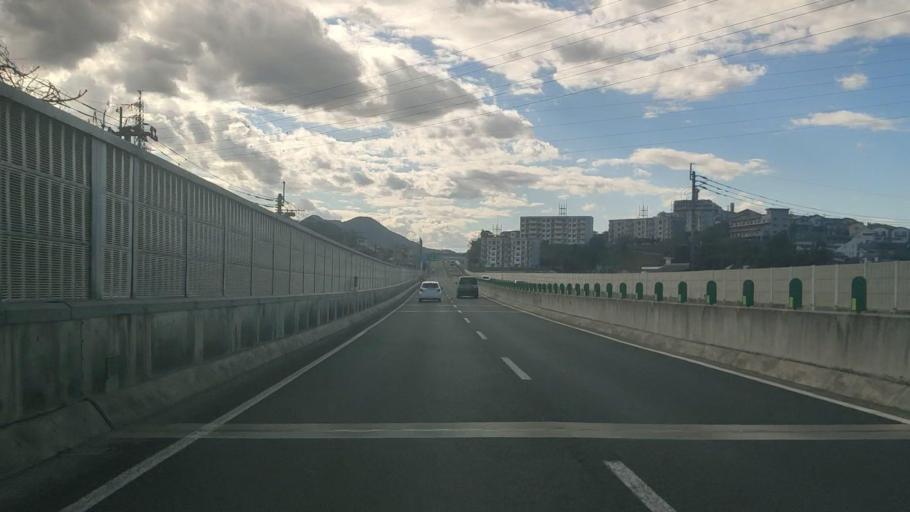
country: JP
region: Yamaguchi
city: Shimonoseki
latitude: 33.9085
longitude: 130.9536
